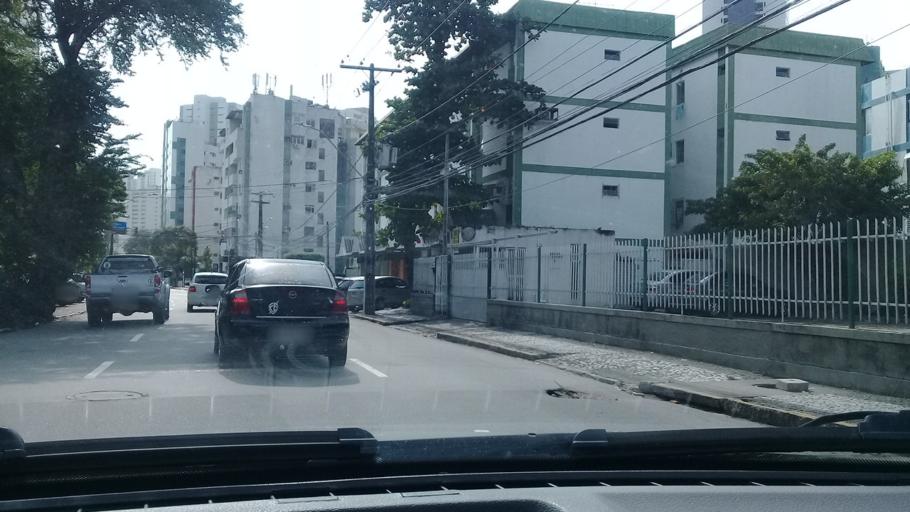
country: BR
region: Pernambuco
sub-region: Recife
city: Recife
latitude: -8.1351
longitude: -34.9070
